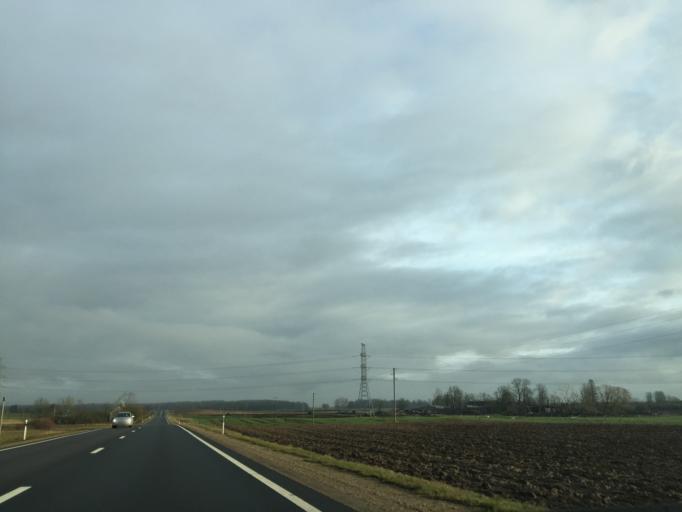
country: LV
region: Durbe
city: Liegi
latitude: 56.5698
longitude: 21.2799
